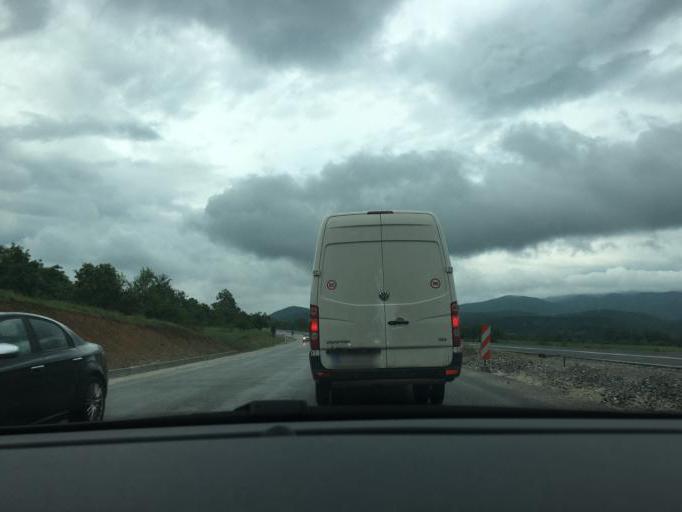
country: MK
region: Debarca
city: Belcista
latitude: 41.3317
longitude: 20.8019
